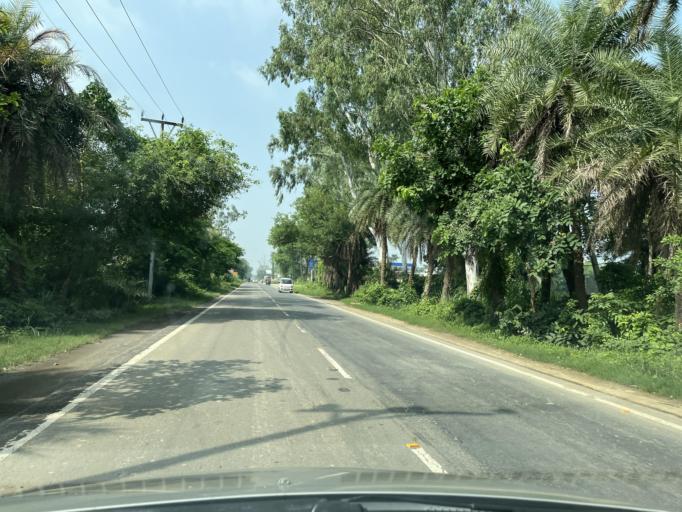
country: IN
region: Uttarakhand
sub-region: Udham Singh Nagar
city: Bazpur
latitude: 29.1726
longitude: 79.1684
